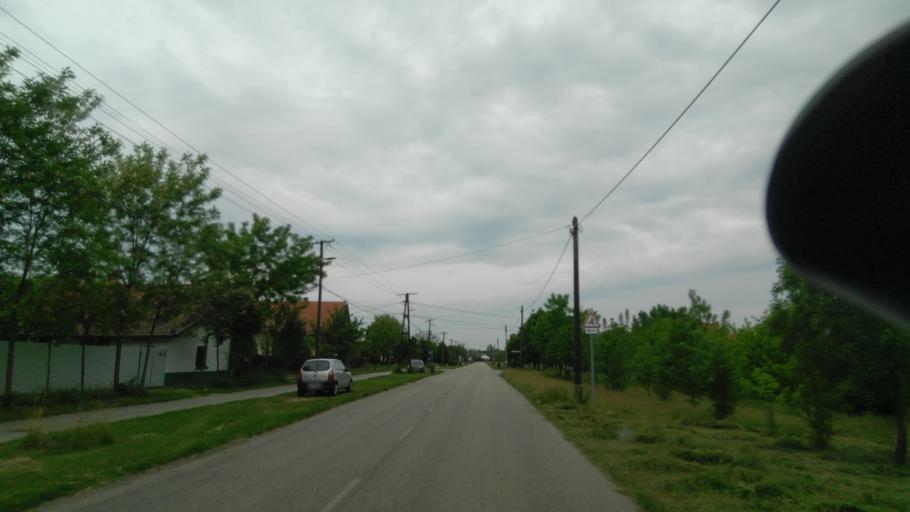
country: HU
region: Bekes
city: Veszto
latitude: 46.9181
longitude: 21.2534
